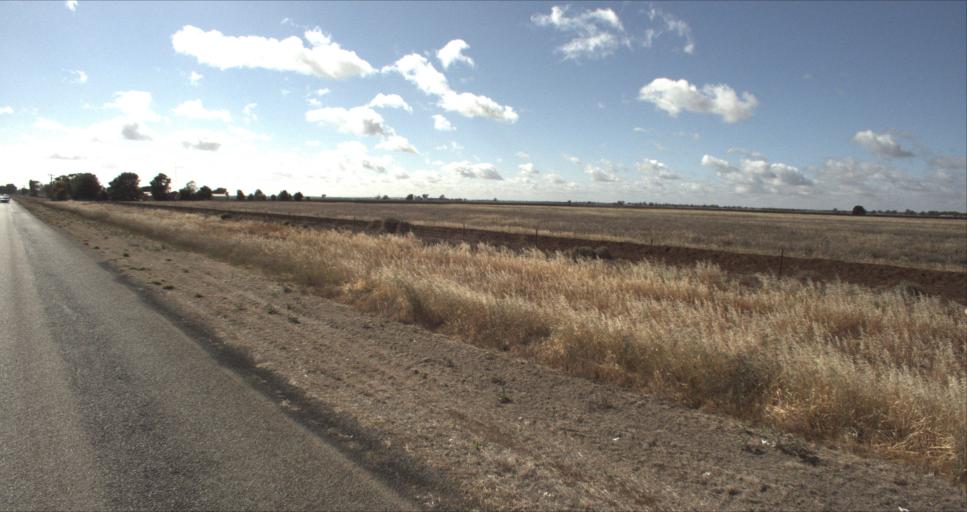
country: AU
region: New South Wales
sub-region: Leeton
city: Leeton
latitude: -34.5519
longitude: 146.3026
